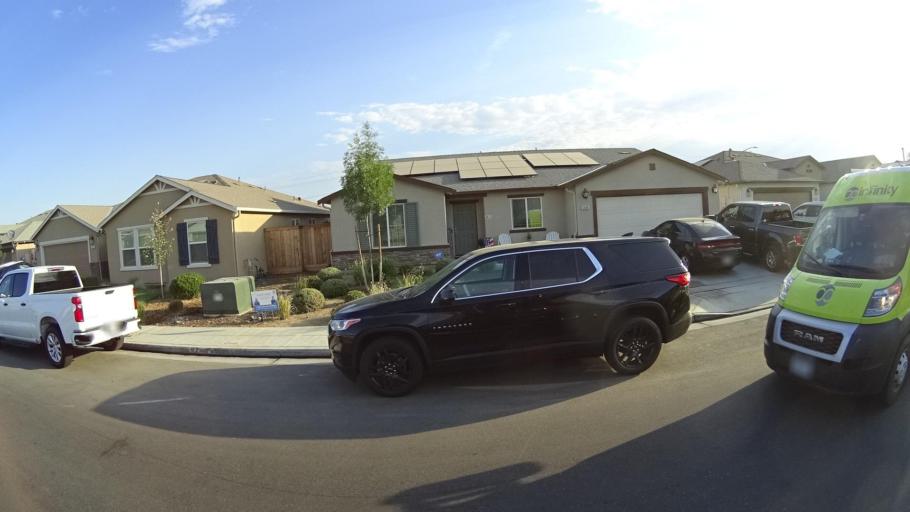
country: US
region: California
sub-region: Fresno County
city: Sunnyside
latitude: 36.7136
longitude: -119.7057
